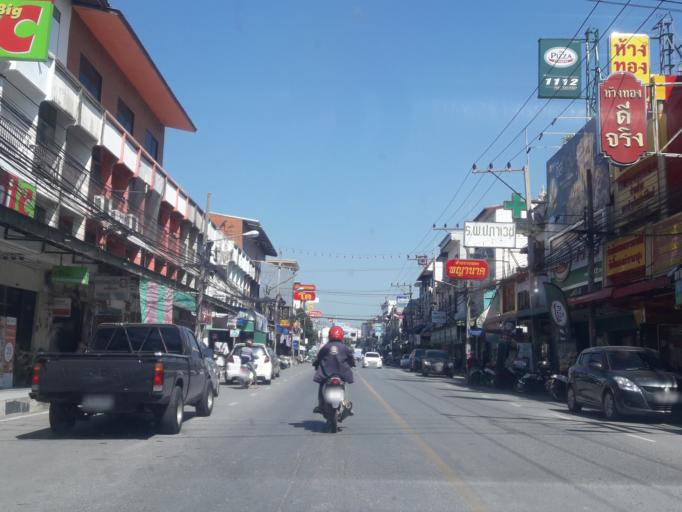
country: TH
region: Sara Buri
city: Nong Khae
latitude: 14.3420
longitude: 100.8670
